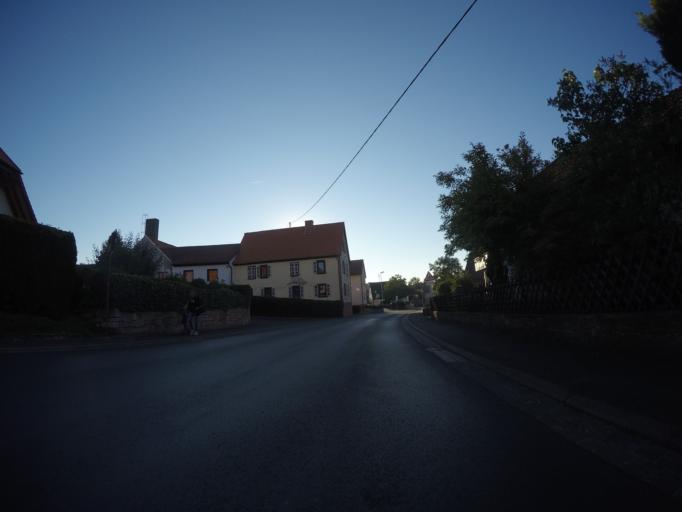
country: DE
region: Bavaria
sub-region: Regierungsbezirk Unterfranken
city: Schollbrunn
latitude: 49.8347
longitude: 9.4651
